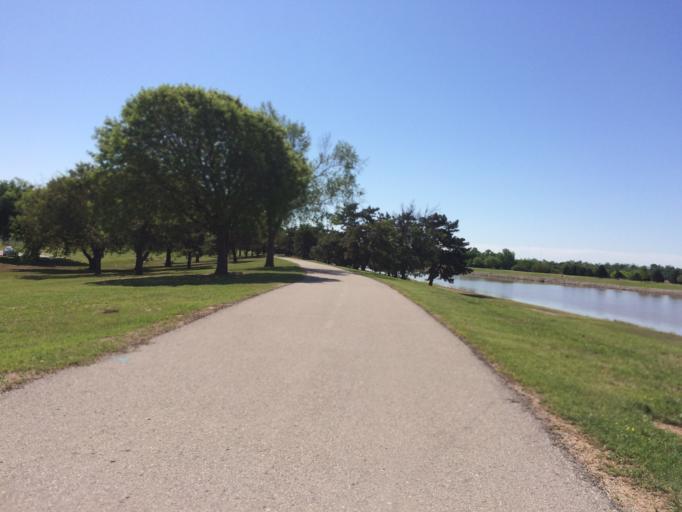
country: US
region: Oklahoma
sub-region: Oklahoma County
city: Oklahoma City
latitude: 35.4529
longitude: -97.5288
